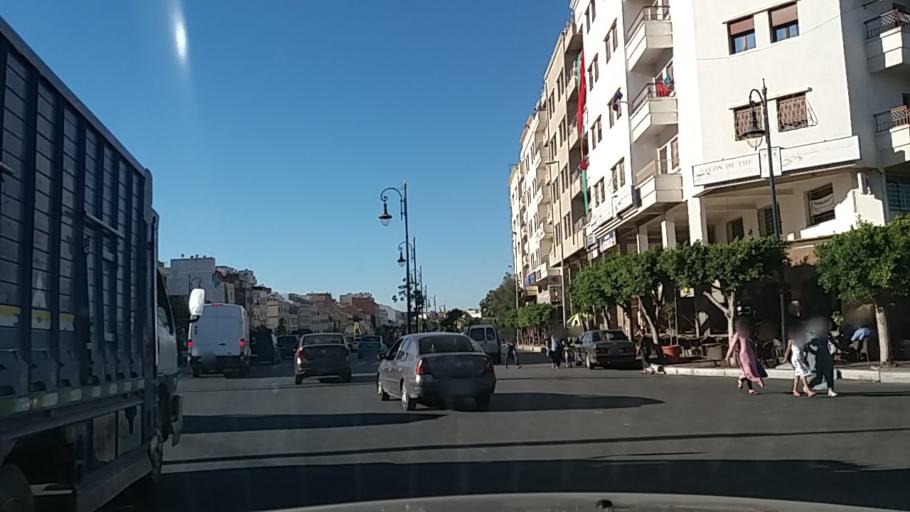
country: MA
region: Tanger-Tetouan
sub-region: Tanger-Assilah
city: Tangier
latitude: 35.7362
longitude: -5.8015
